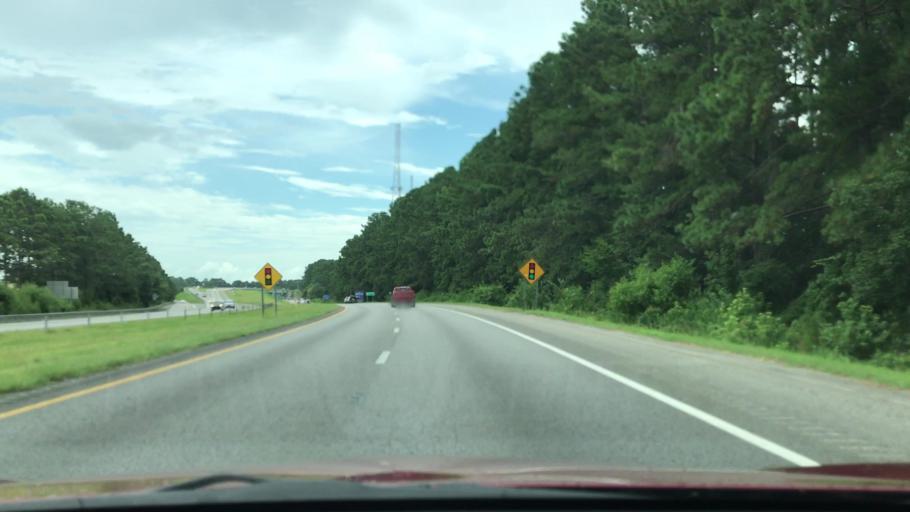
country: US
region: South Carolina
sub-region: Charleston County
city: Shell Point
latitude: 32.7977
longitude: -80.0353
